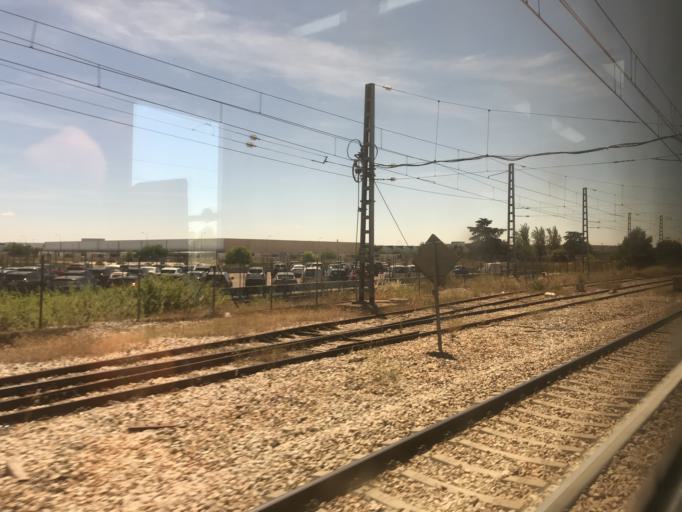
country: ES
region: Madrid
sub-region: Provincia de Madrid
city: Getafe
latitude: 40.3081
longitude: -3.7078
